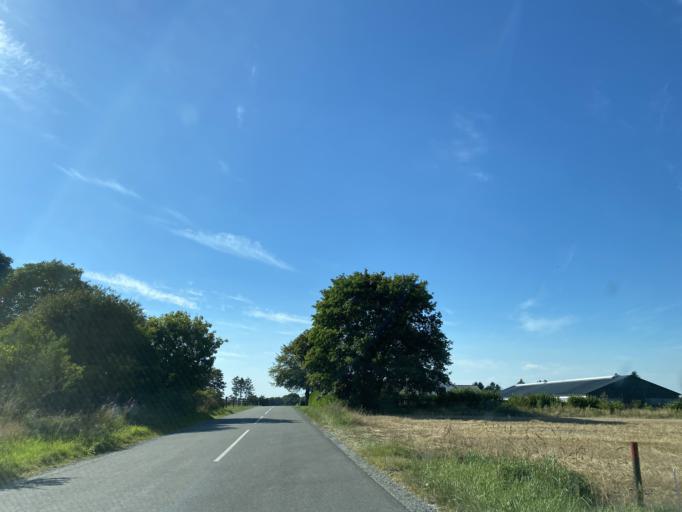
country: DK
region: South Denmark
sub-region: Vejle Kommune
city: Give
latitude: 55.8926
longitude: 9.2816
